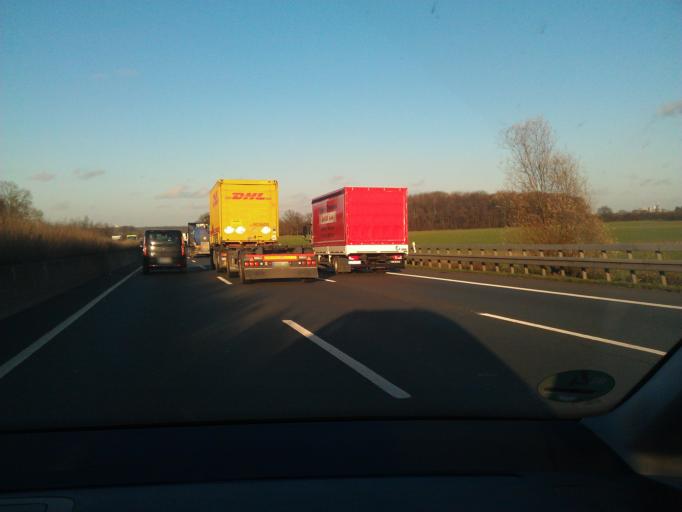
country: DE
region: North Rhine-Westphalia
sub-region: Regierungsbezirk Munster
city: Beckum
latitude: 51.7368
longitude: 7.9878
